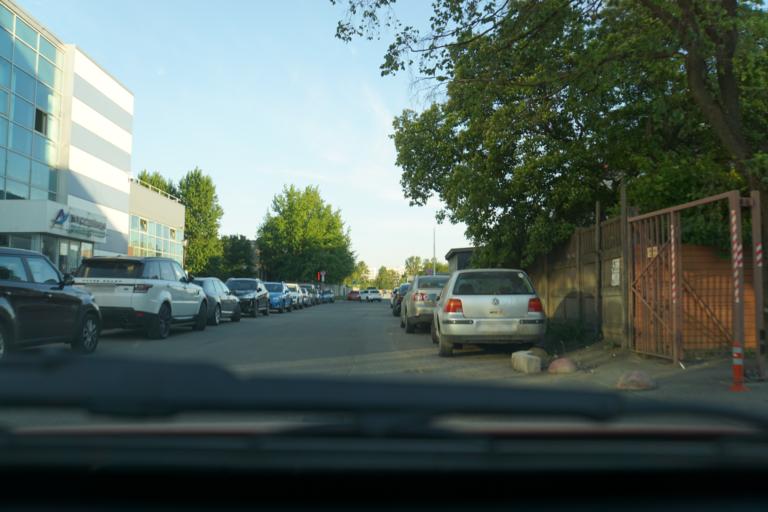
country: RU
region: St.-Petersburg
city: Avtovo
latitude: 59.8652
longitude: 30.2578
